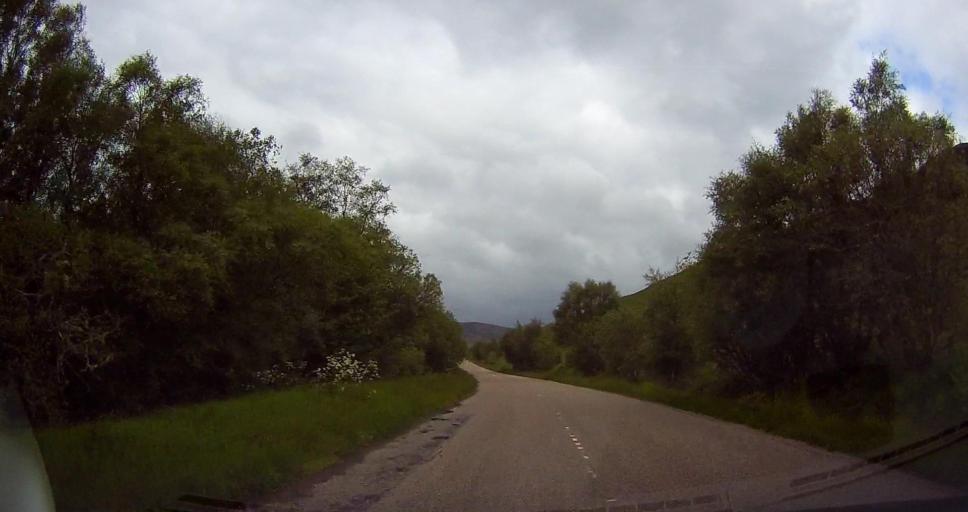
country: GB
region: Scotland
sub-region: Highland
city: Dornoch
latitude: 58.0049
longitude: -4.2237
